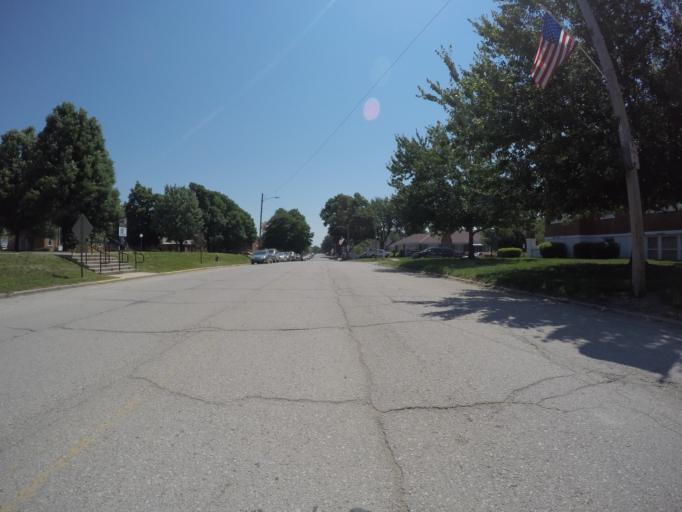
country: US
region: Kansas
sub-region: Doniphan County
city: Highland
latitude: 39.8595
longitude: -95.2714
